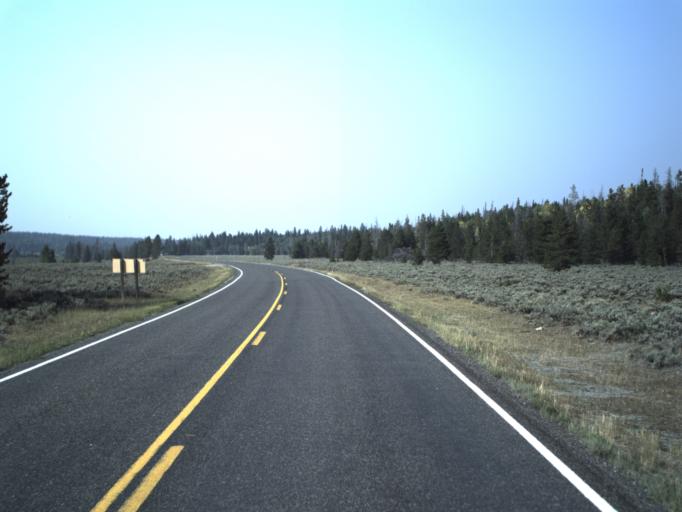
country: US
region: Wyoming
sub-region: Uinta County
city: Evanston
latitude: 40.8769
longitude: -110.8312
